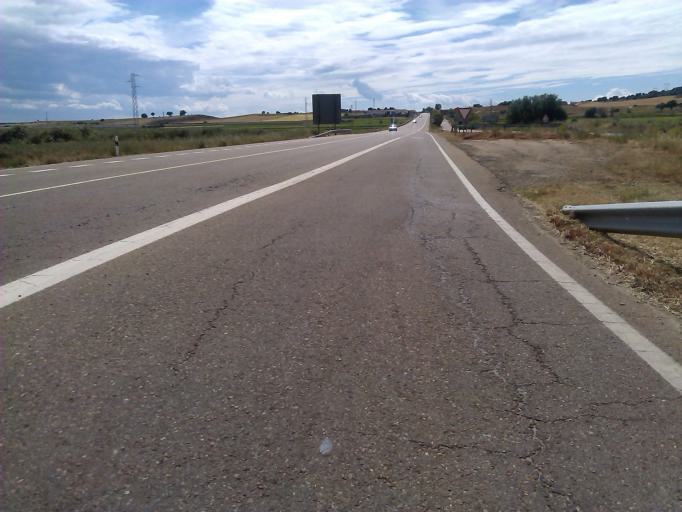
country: ES
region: Castille and Leon
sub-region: Provincia de Leon
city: Villarejo de Orbigo
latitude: 42.4519
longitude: -5.9209
